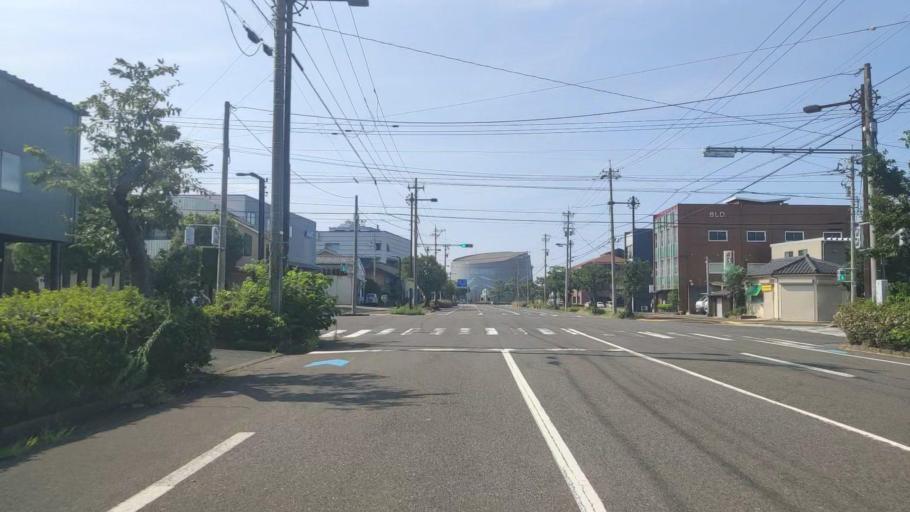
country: JP
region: Fukui
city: Tsuruga
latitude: 35.6577
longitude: 136.0727
